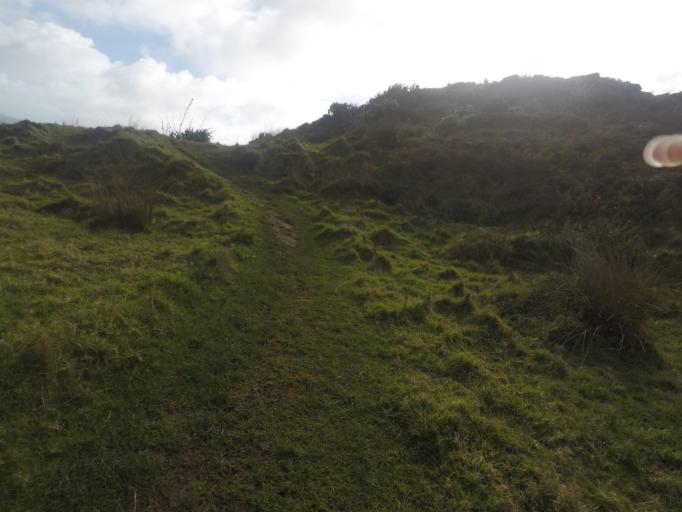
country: NZ
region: Auckland
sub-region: Auckland
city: Muriwai Beach
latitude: -36.8694
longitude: 174.4355
